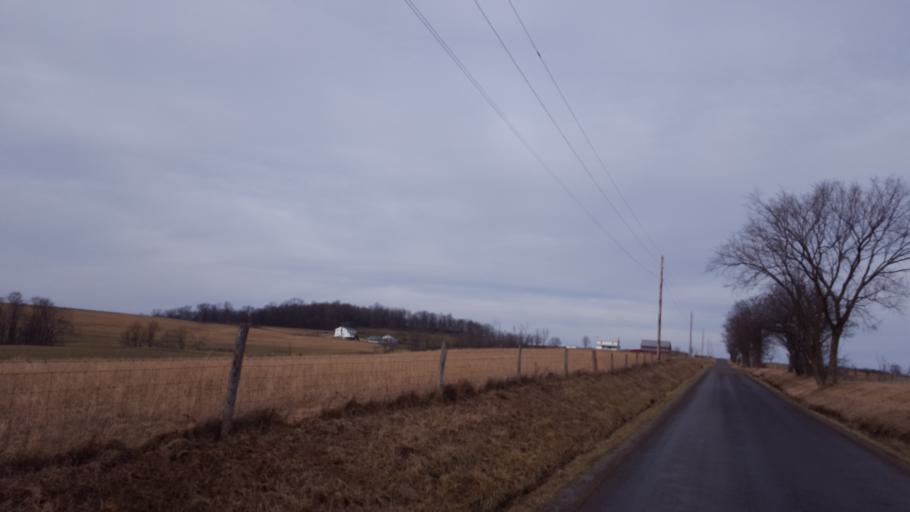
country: US
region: Ohio
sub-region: Holmes County
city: Millersburg
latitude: 40.6341
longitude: -81.8517
